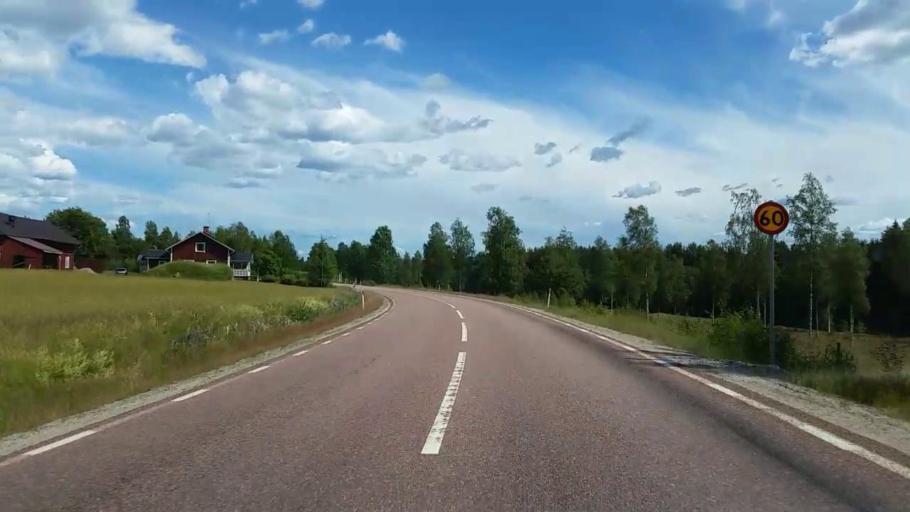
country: SE
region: Gaevleborg
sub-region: Ovanakers Kommun
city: Edsbyn
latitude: 61.3468
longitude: 15.5974
